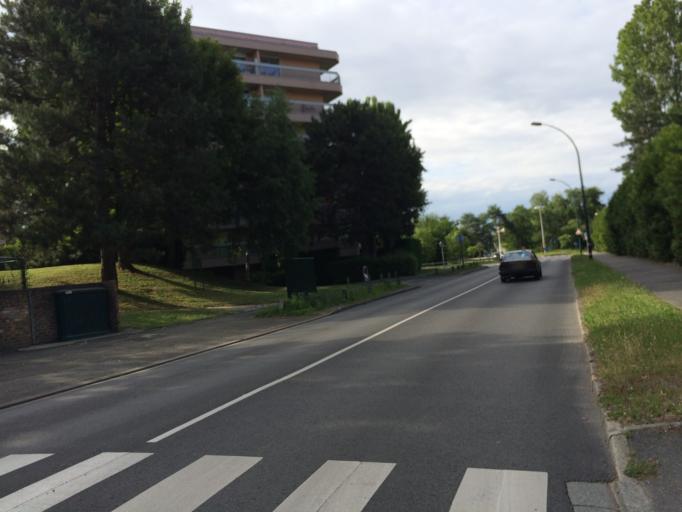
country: FR
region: Ile-de-France
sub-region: Departement de l'Essonne
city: Verrieres-le-Buisson
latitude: 48.7501
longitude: 2.2721
